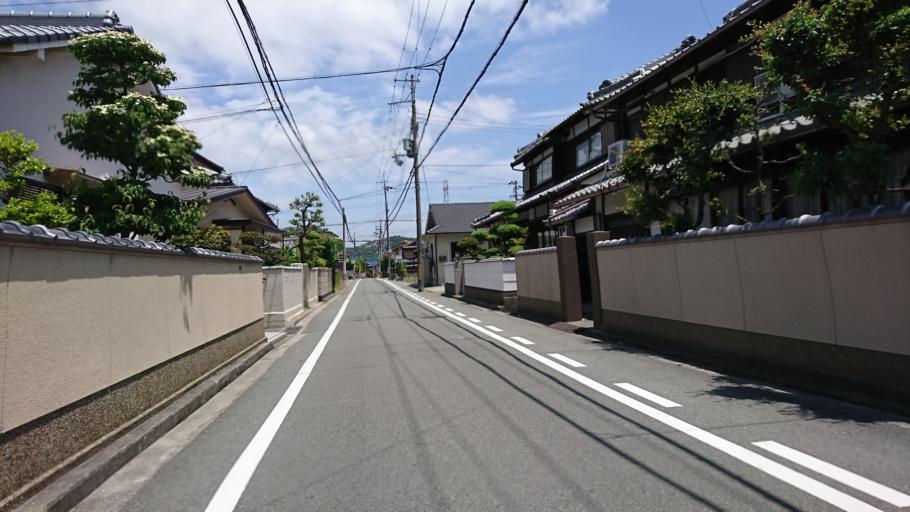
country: JP
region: Hyogo
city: Kakogawacho-honmachi
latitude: 34.7938
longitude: 134.7805
